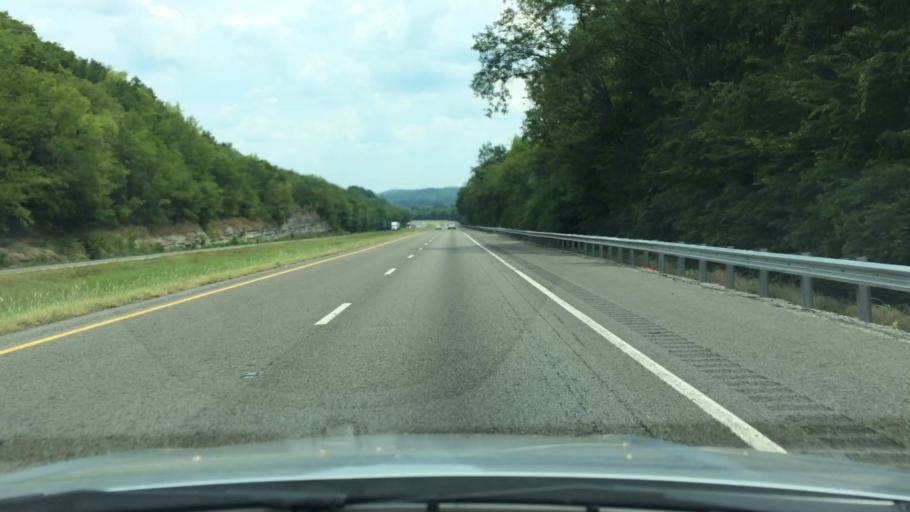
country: US
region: Tennessee
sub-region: Marshall County
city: Cornersville
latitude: 35.4060
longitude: -86.8802
